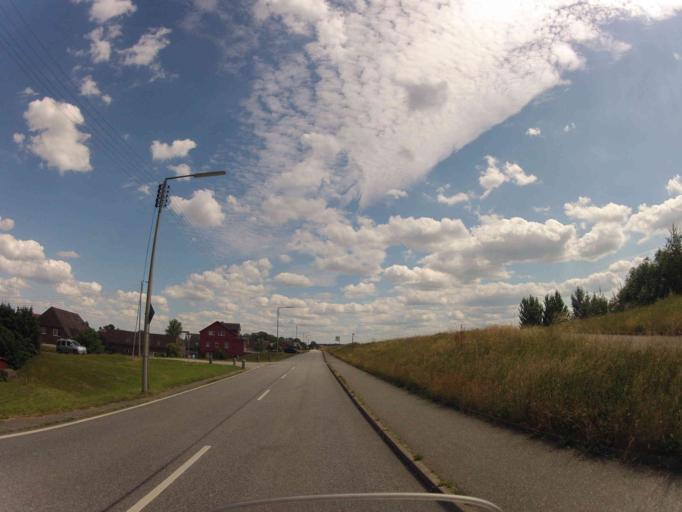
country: DE
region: Lower Saxony
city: Stelle
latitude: 53.4228
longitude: 10.1402
